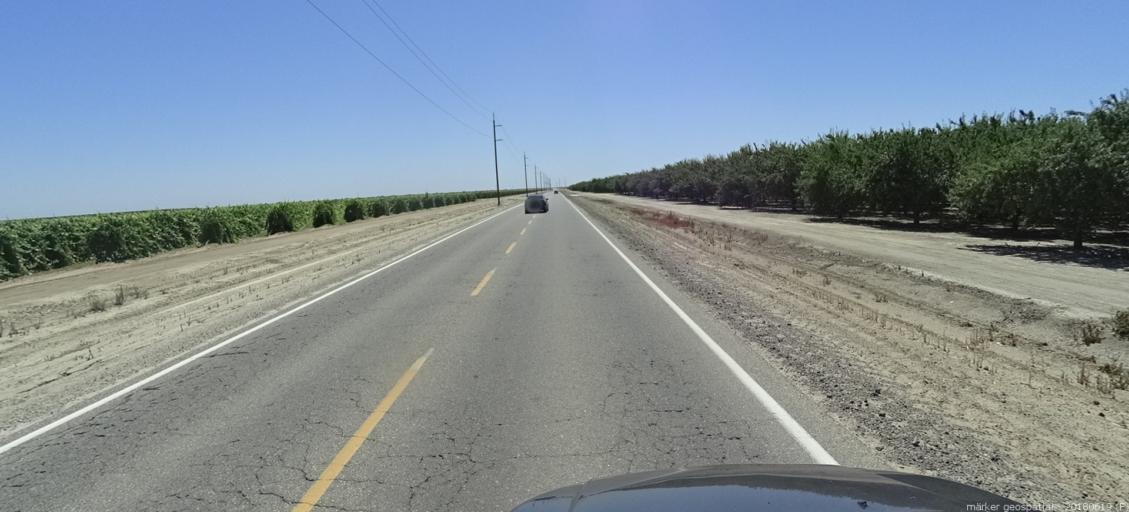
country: US
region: California
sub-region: Fresno County
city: Mendota
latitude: 36.8553
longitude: -120.3297
